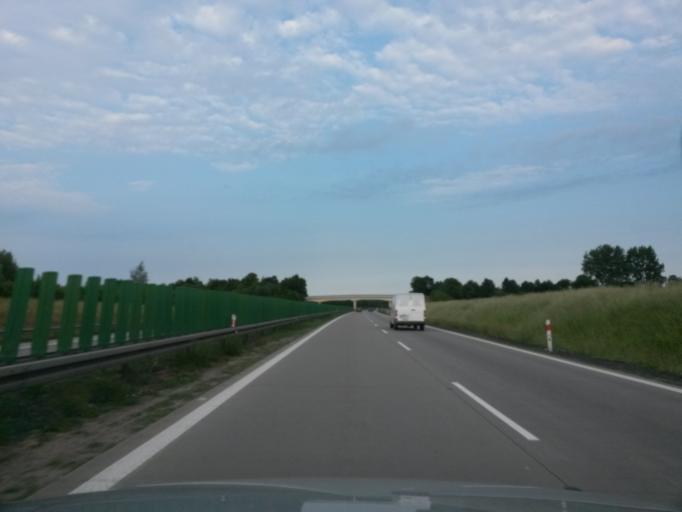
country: PL
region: Lower Silesian Voivodeship
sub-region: Powiat wroclawski
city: Katy Wroclawskie
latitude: 51.0288
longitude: 16.6566
